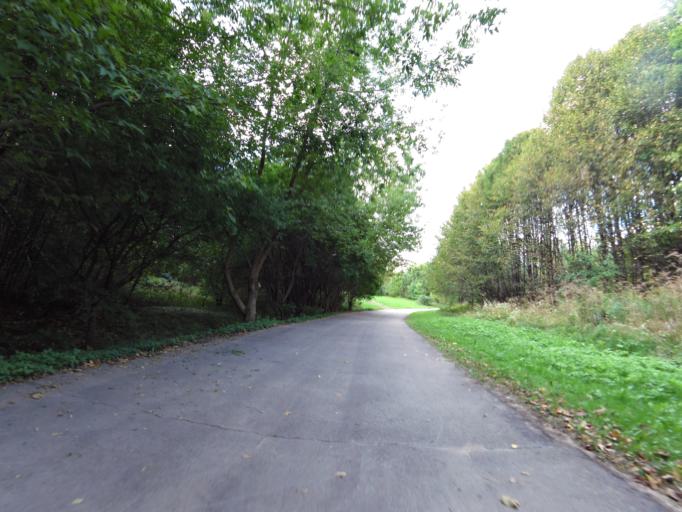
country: LT
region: Vilnius County
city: Seskine
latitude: 54.7084
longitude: 25.2464
